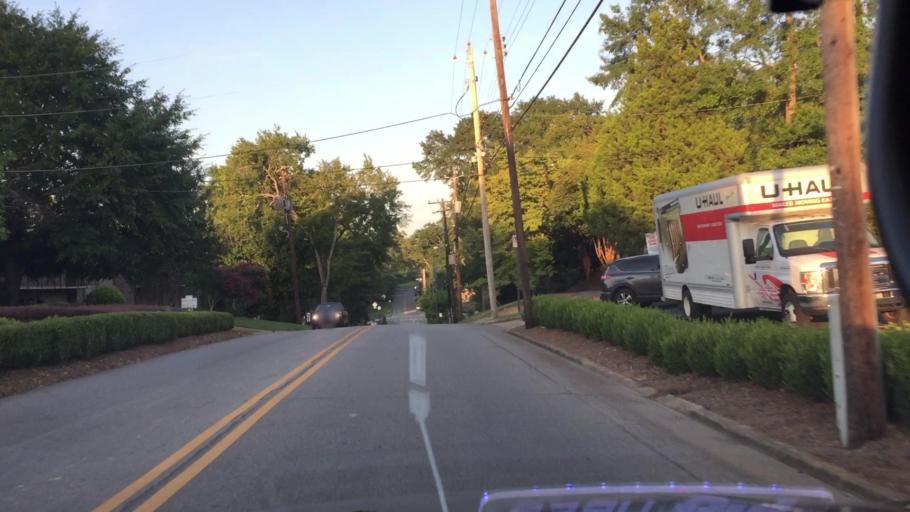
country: US
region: Alabama
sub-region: Lee County
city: Auburn
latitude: 32.6065
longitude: -85.4775
